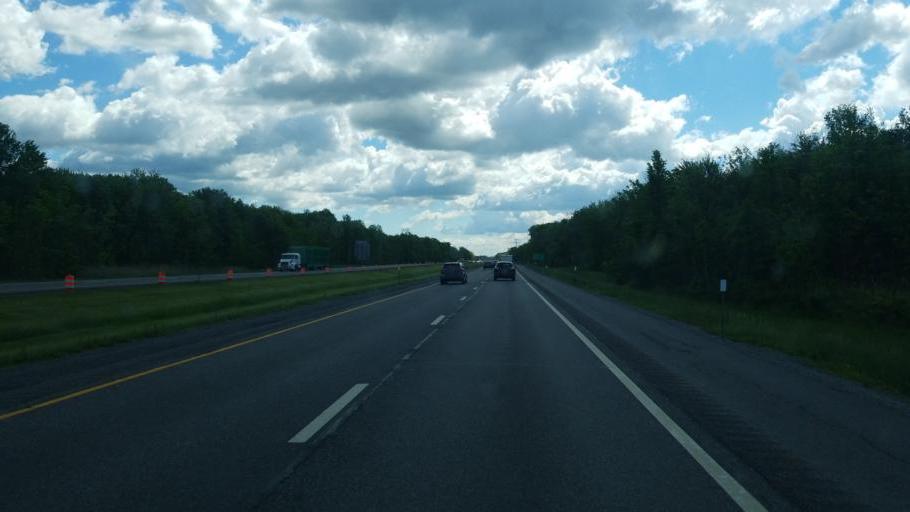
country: US
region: New York
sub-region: Onondaga County
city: Minoa
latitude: 43.0947
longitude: -76.0199
